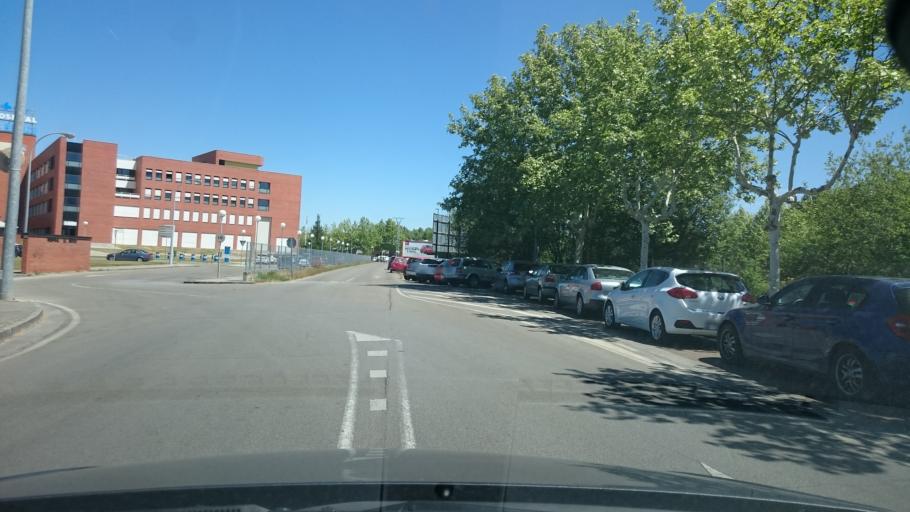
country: ES
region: Castille and Leon
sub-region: Provincia de Leon
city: Camponaraya
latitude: 42.5700
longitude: -6.6436
